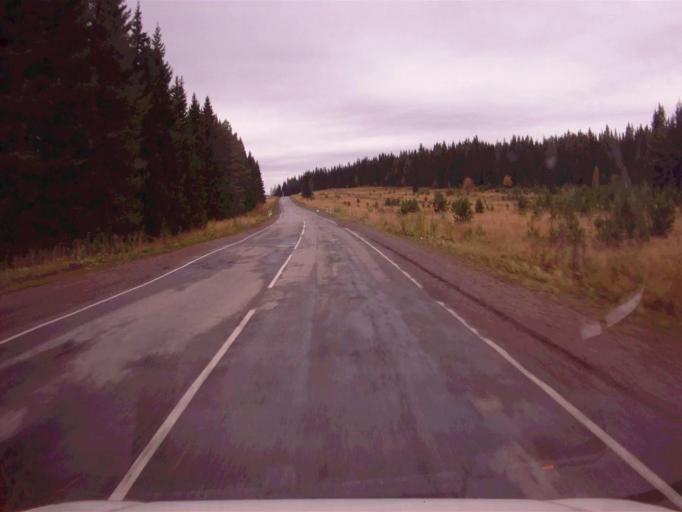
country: RU
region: Chelyabinsk
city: Nyazepetrovsk
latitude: 56.0664
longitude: 59.6446
